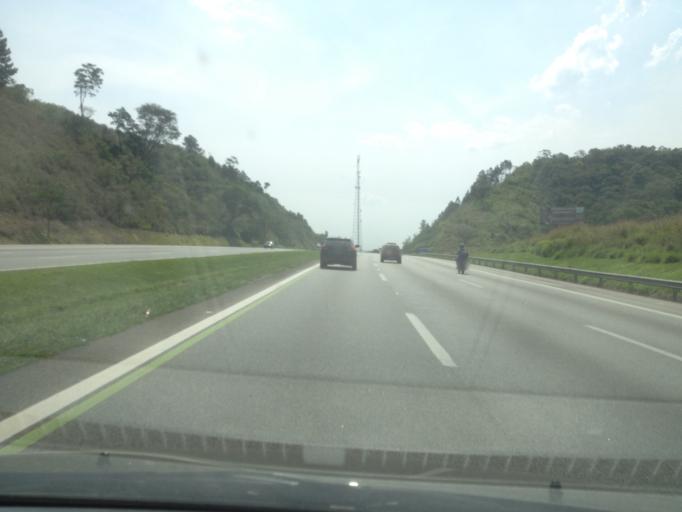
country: BR
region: Sao Paulo
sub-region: Sao Roque
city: Sao Roque
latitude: -23.4383
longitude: -47.1150
